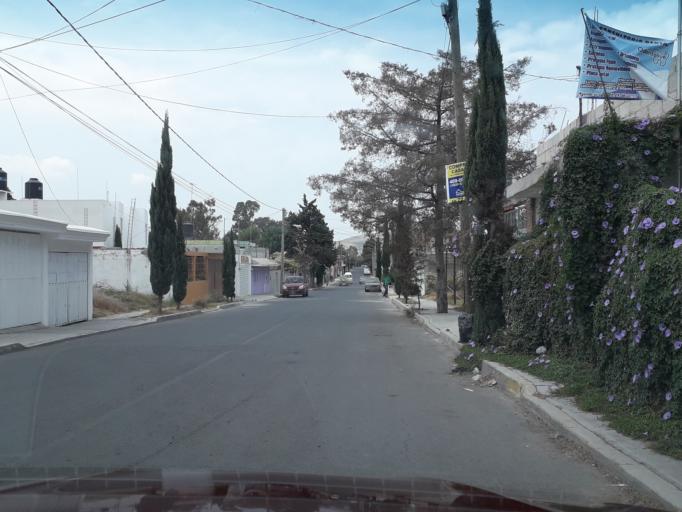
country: MX
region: Puebla
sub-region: Puebla
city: El Capulo (La Quebradora)
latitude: 18.9680
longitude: -98.2592
